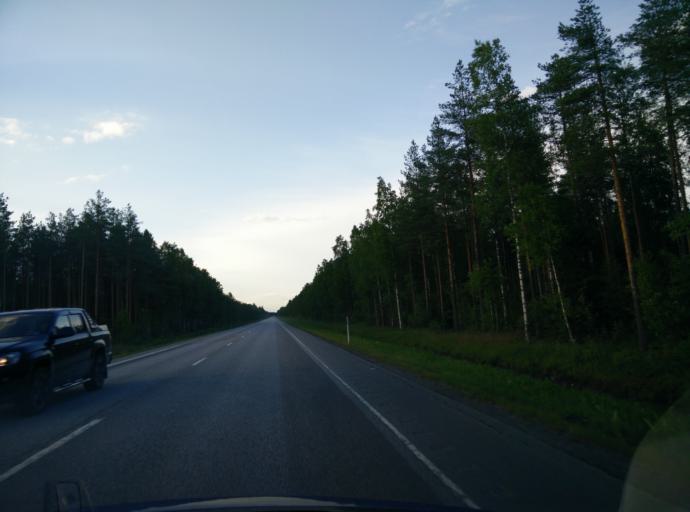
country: FI
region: Northern Ostrobothnia
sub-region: Haapavesi-Siikalatva
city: Pulkkila
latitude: 64.1294
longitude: 25.8002
